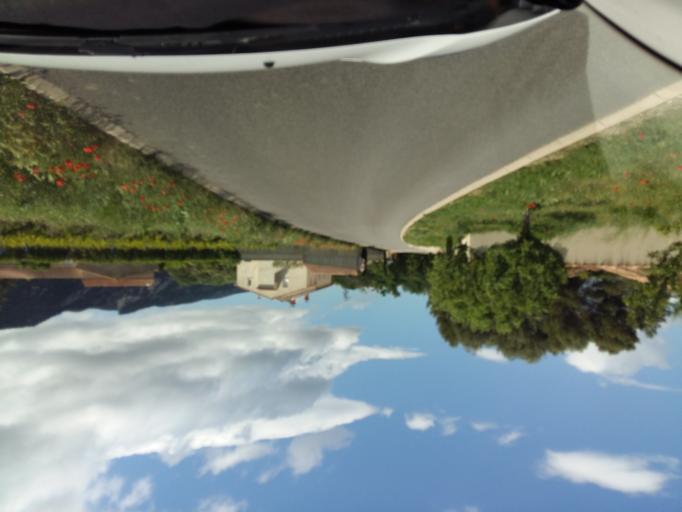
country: FR
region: Provence-Alpes-Cote d'Azur
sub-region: Departement du Vaucluse
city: Maubec
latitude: 43.8464
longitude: 5.1341
